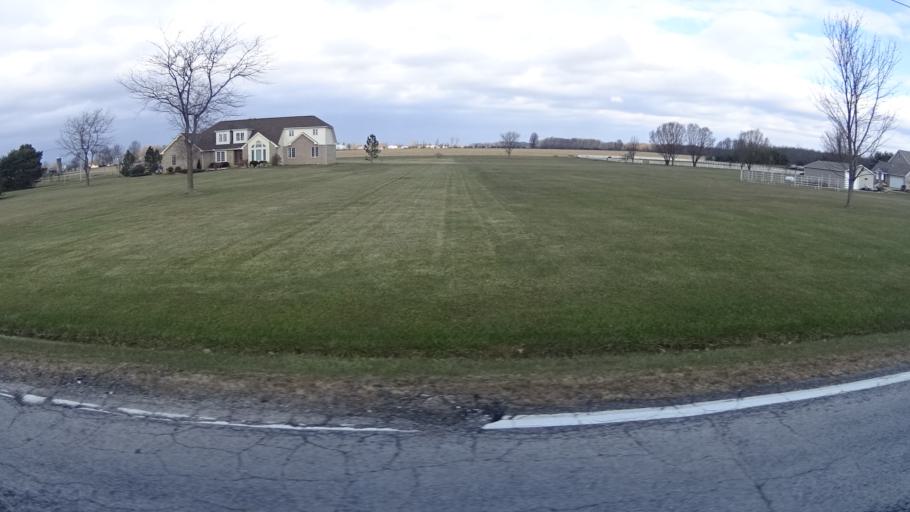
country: US
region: Ohio
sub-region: Lorain County
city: Camden
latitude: 41.2050
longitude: -82.3033
